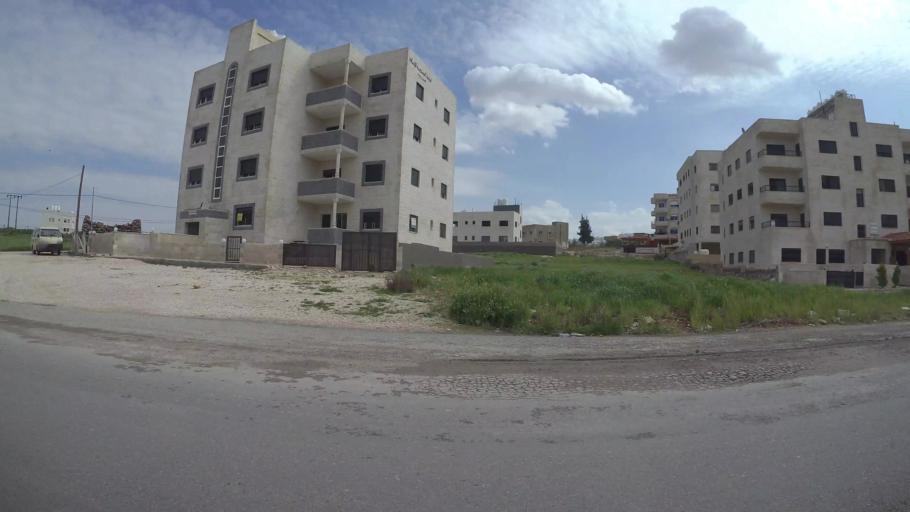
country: JO
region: Amman
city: Al Jubayhah
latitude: 32.0676
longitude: 35.8301
